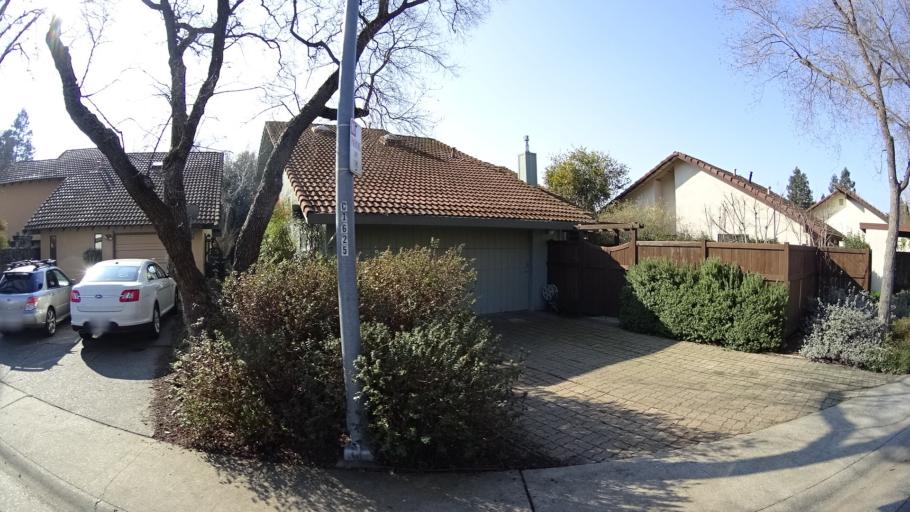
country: US
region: California
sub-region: Yolo County
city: Davis
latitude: 38.5505
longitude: -121.7813
